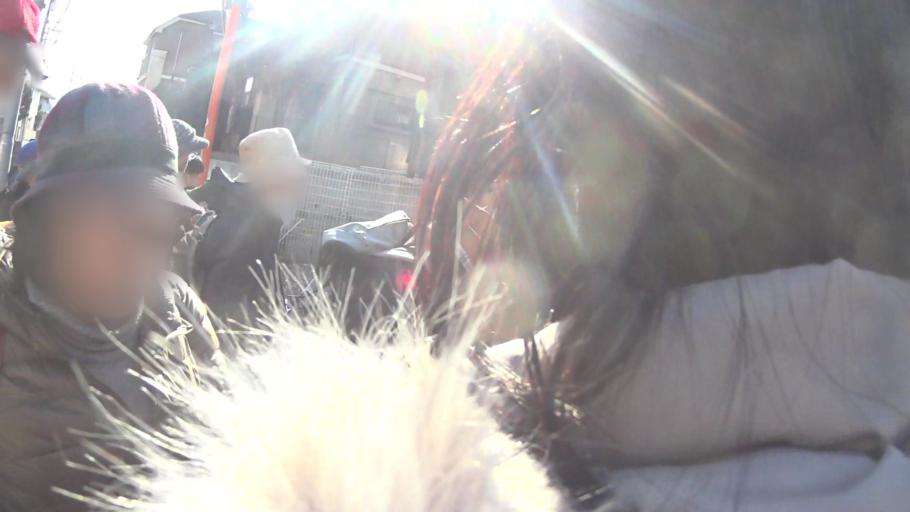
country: JP
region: Tokyo
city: Mitaka-shi
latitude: 35.6535
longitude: 139.6047
